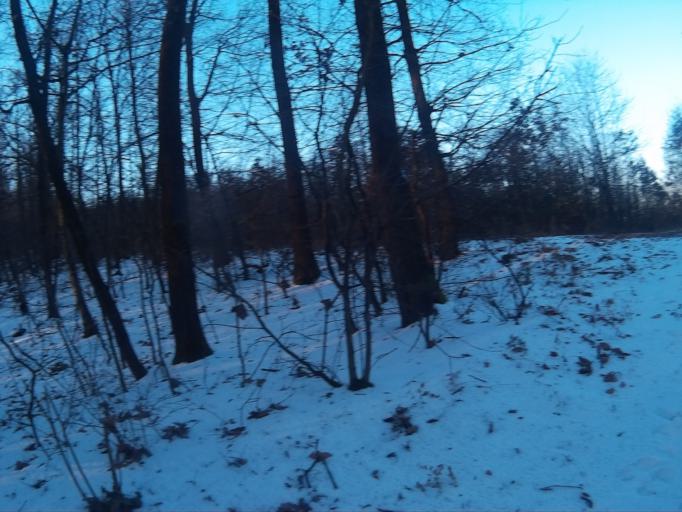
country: HU
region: Borsod-Abauj-Zemplen
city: Putnok
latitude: 48.3351
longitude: 20.4261
